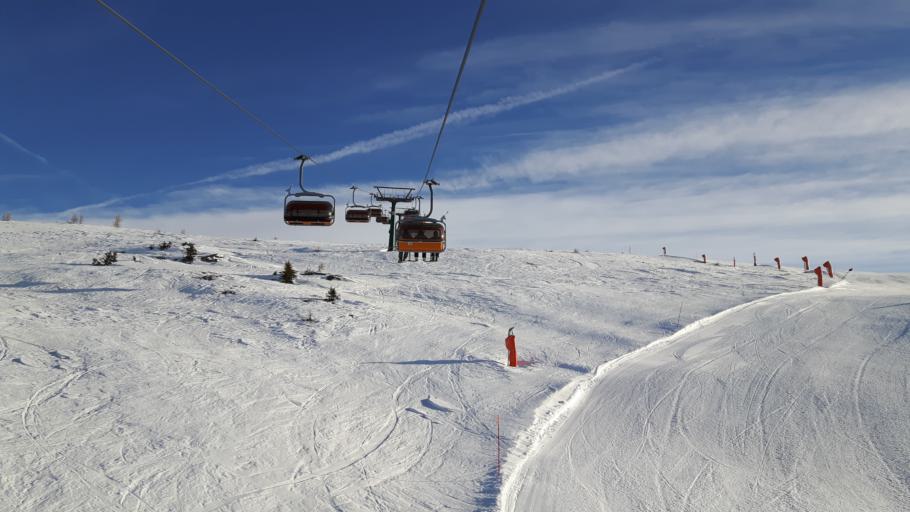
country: IT
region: Trentino-Alto Adige
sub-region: Provincia di Trento
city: Moena
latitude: 46.3401
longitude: 11.7138
